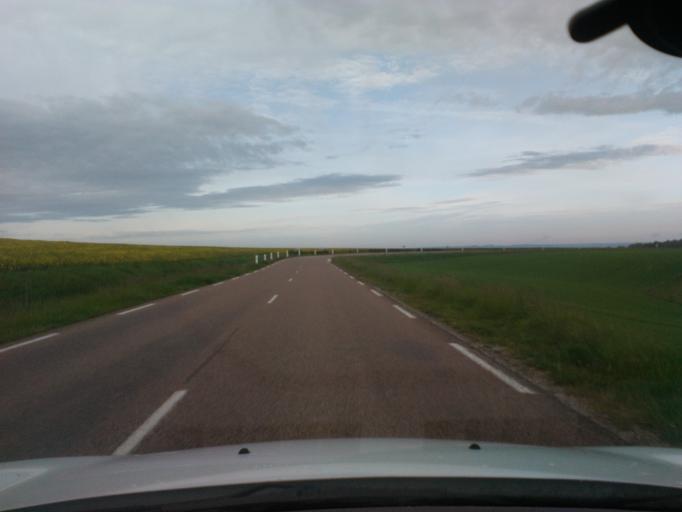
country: FR
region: Champagne-Ardenne
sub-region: Departement de la Haute-Marne
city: Lavilleneuve-au-Roi
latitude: 48.2267
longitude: 4.8786
